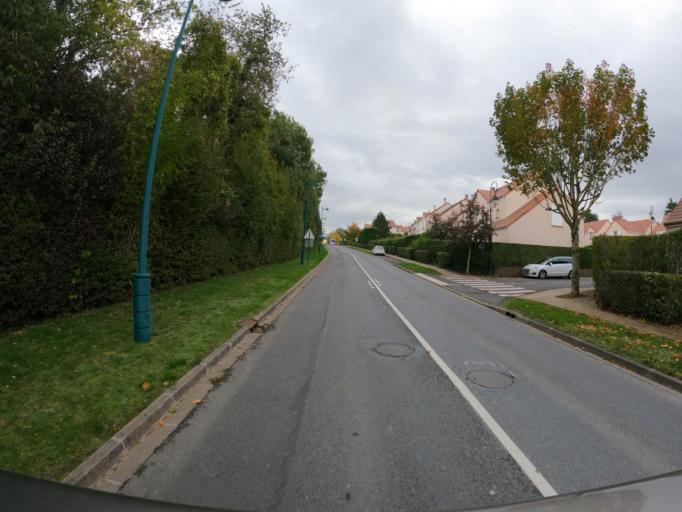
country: FR
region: Ile-de-France
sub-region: Departement de Seine-et-Marne
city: Magny-le-Hongre
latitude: 48.8647
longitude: 2.8165
